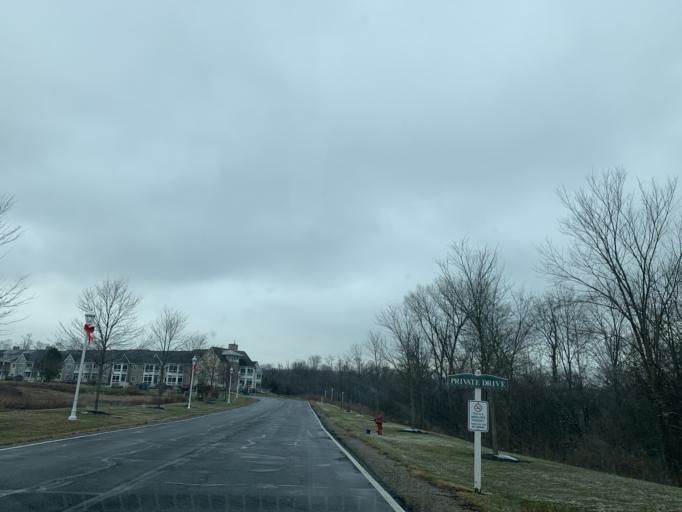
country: US
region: Ohio
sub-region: Licking County
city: Granville South
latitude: 40.0557
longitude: -82.5375
